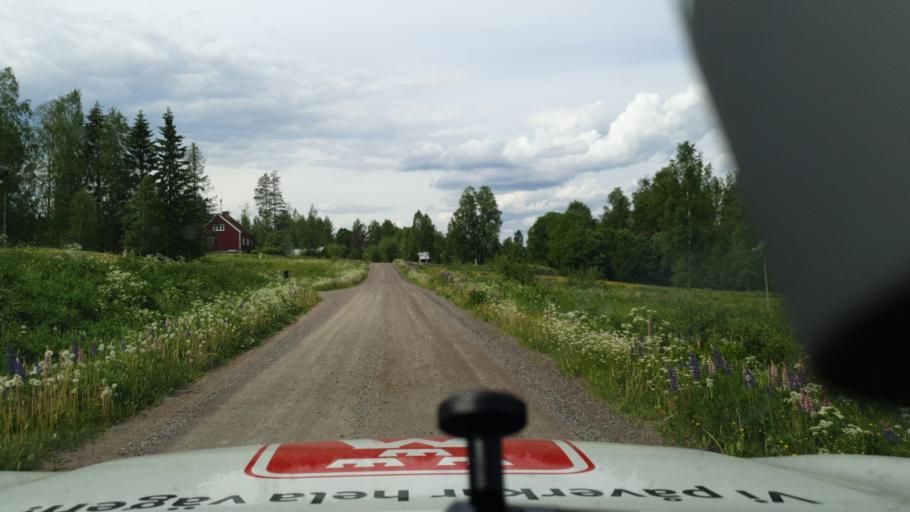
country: SE
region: Vaermland
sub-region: Torsby Kommun
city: Torsby
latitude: 59.9718
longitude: 12.8636
